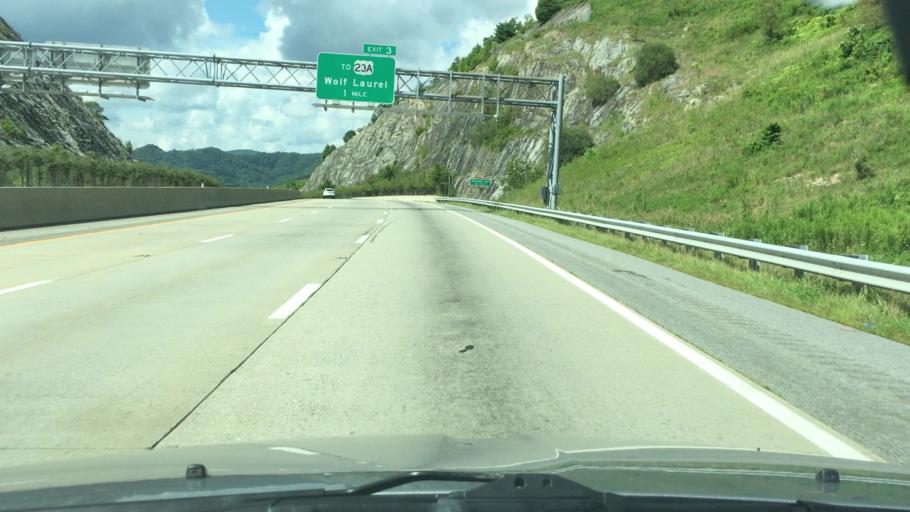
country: US
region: North Carolina
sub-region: Madison County
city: Mars Hill
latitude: 35.8930
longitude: -82.5437
